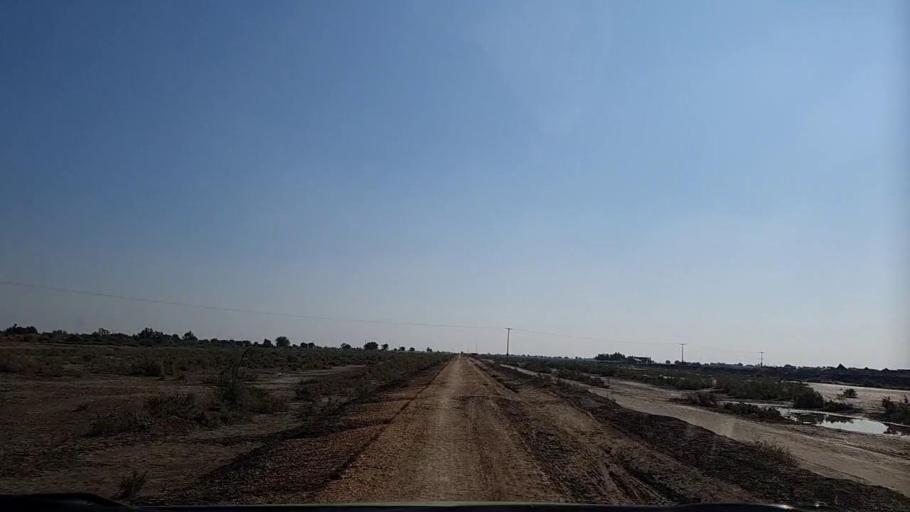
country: PK
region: Sindh
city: Pithoro
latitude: 25.7048
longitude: 69.3376
